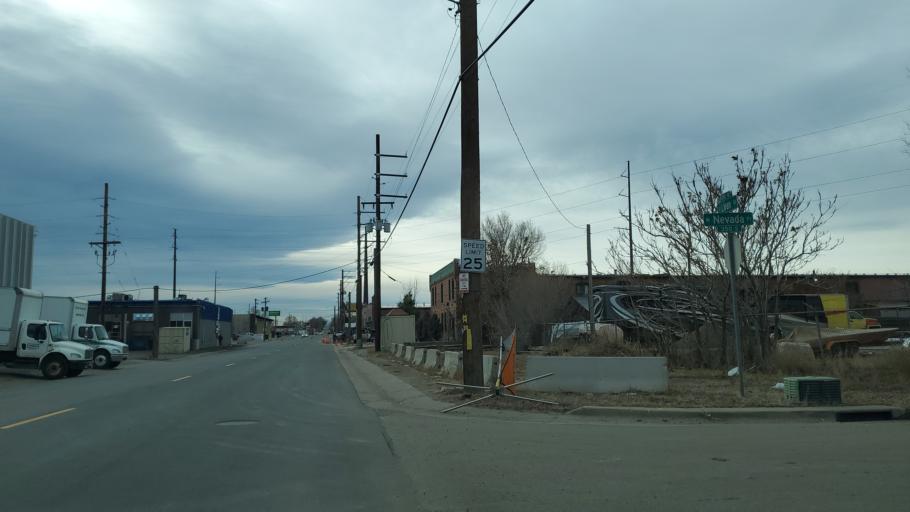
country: US
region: Colorado
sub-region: Denver County
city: Denver
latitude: 39.7103
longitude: -105.0016
